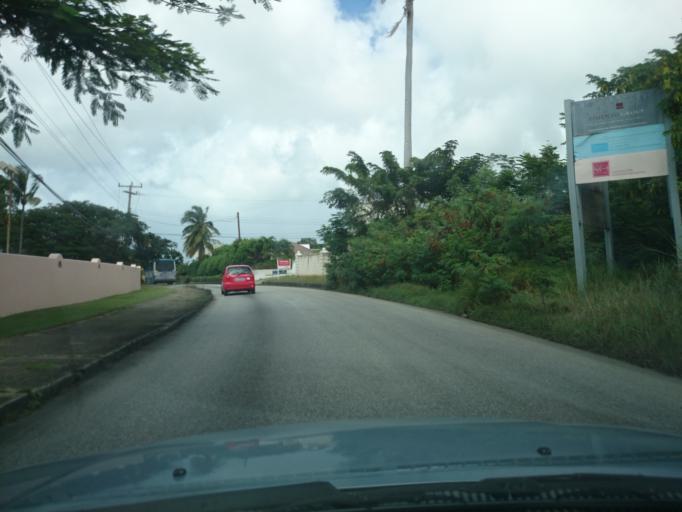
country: BB
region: Saint James
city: Holetown
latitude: 13.2028
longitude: -59.6396
